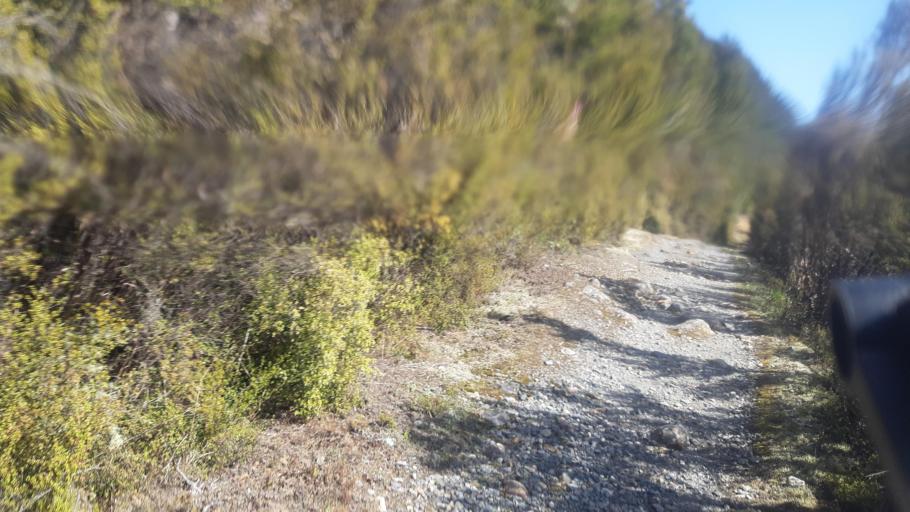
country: NZ
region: Tasman
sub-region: Tasman District
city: Wakefield
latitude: -41.8001
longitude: 172.8388
